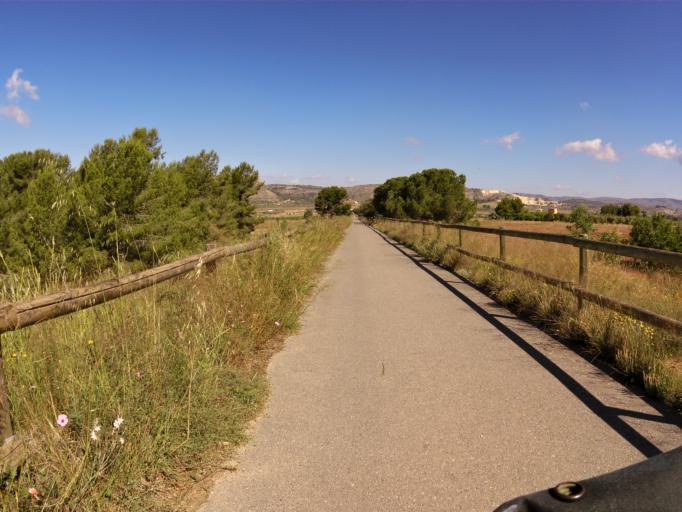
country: ES
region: Valencia
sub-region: Provincia de Alicante
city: Biar
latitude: 38.6357
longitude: -0.8036
